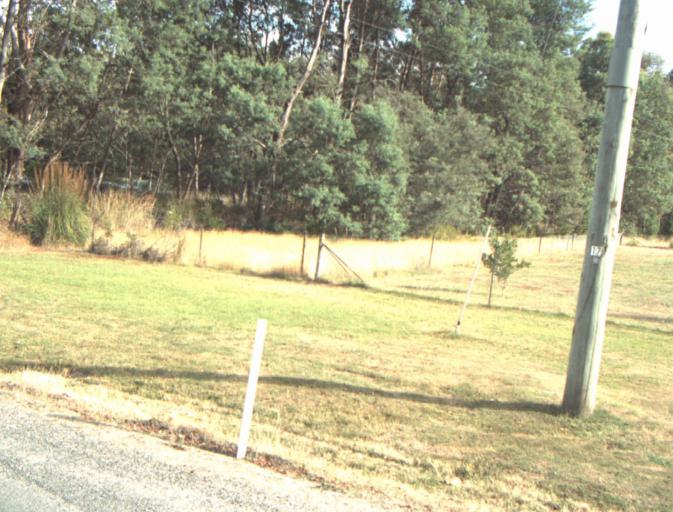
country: AU
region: Tasmania
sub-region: Launceston
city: Mayfield
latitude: -41.2688
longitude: 147.1668
